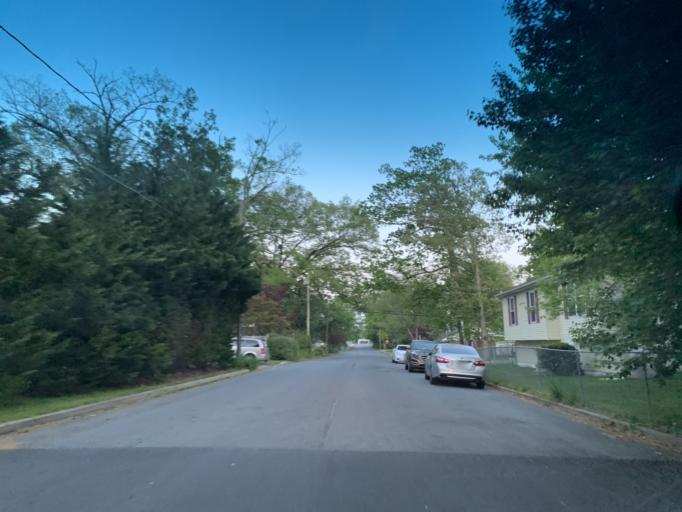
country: US
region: Maryland
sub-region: Harford County
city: Aberdeen
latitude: 39.5056
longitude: -76.1716
